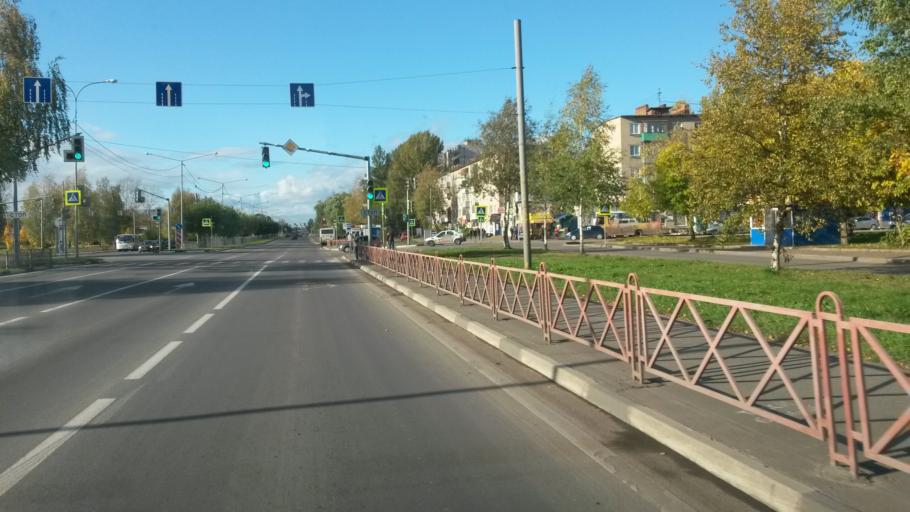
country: RU
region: Jaroslavl
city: Yaroslavl
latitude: 57.5676
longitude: 39.9277
